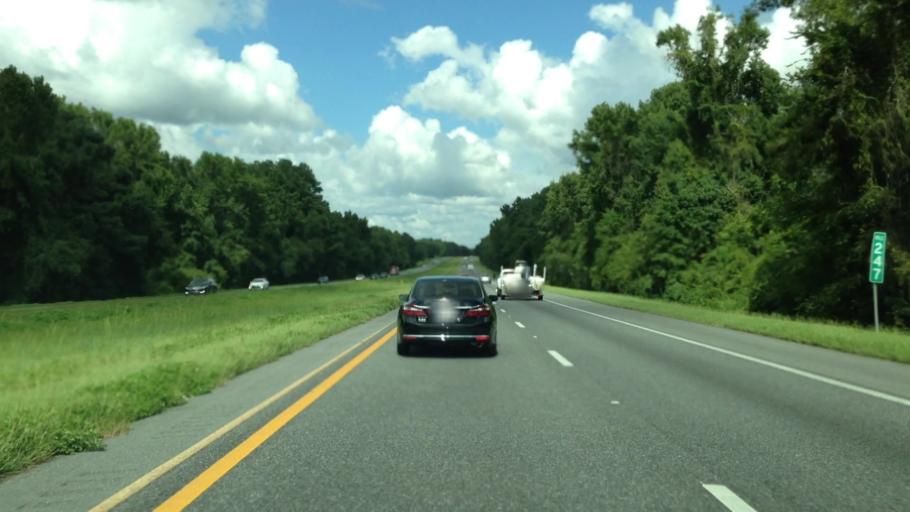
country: US
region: Florida
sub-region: Madison County
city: Madison
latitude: 30.4344
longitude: -83.5311
